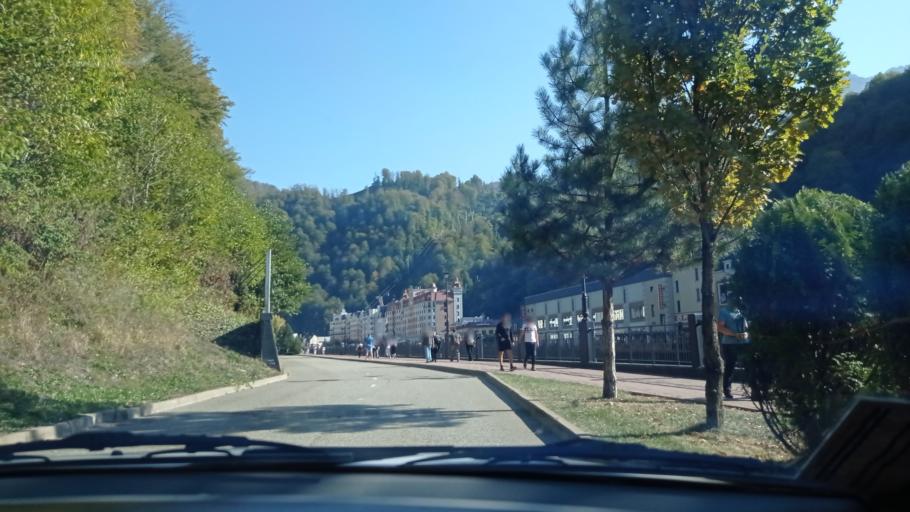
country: RU
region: Krasnodarskiy
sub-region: Sochi City
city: Krasnaya Polyana
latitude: 43.6743
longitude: 40.2899
